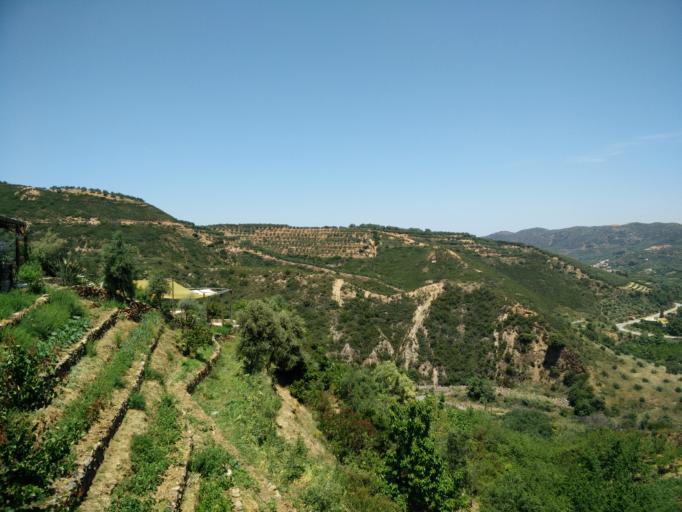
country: GR
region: Crete
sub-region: Nomos Chanias
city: Galatas
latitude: 35.4185
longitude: 23.9398
